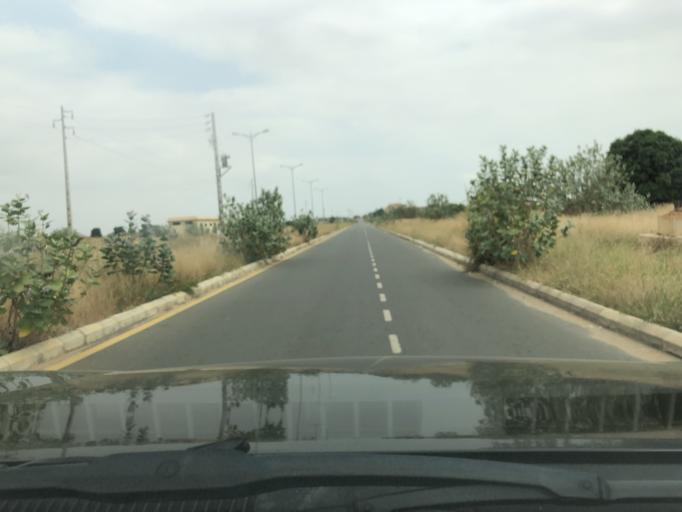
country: AO
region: Luanda
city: Luanda
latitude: -8.9546
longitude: 13.2509
